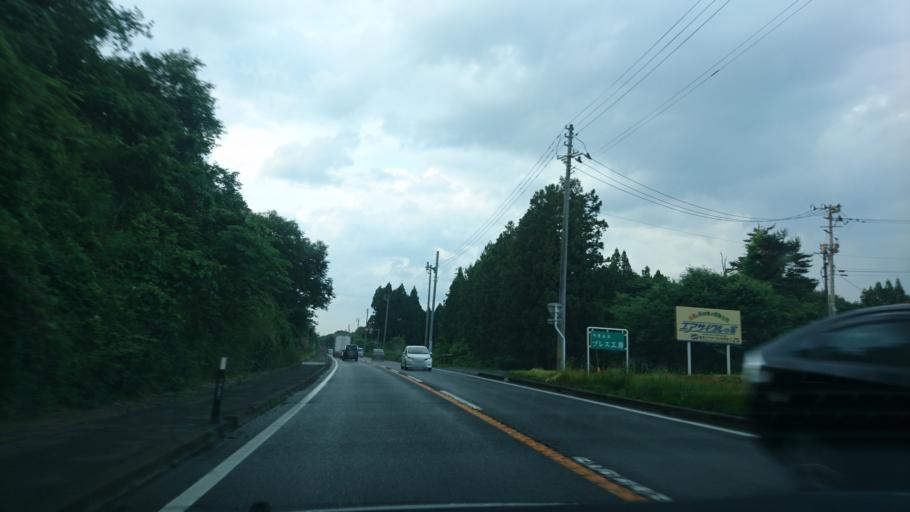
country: JP
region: Iwate
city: Ichinoseki
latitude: 38.9524
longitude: 141.1213
